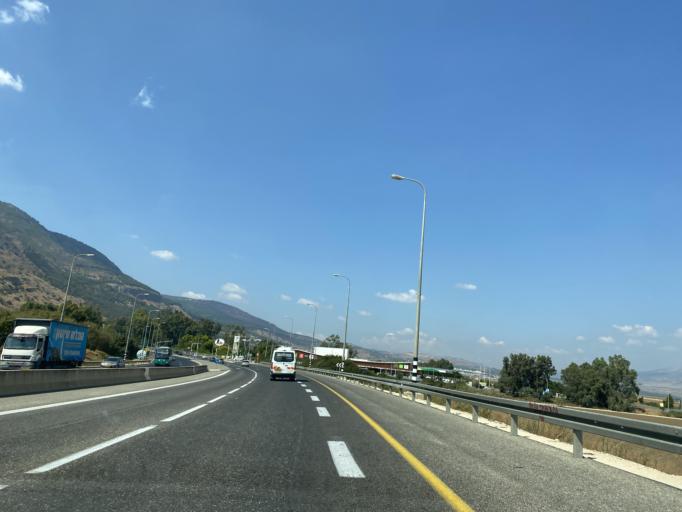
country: IL
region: Northern District
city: Qiryat Shemona
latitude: 33.1677
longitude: 35.5705
